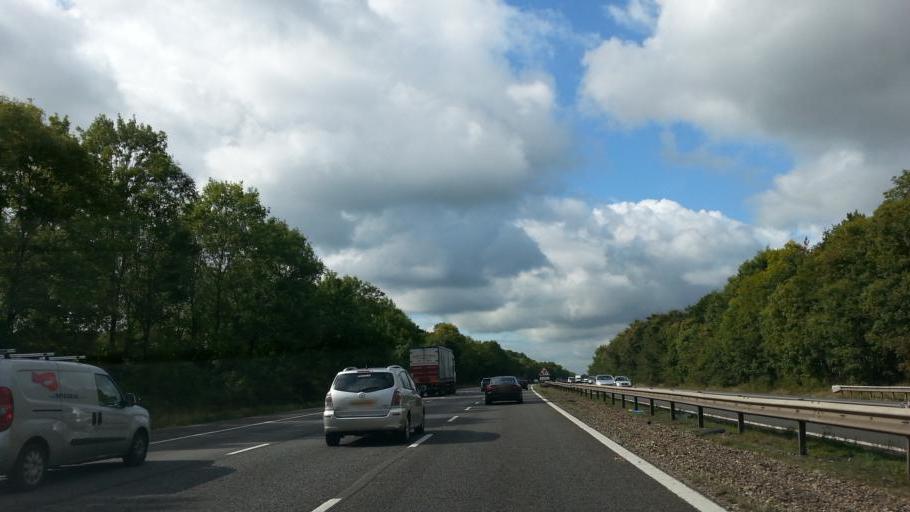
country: GB
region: England
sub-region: Bracknell Forest
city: Binfield
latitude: 51.4531
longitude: -0.8042
